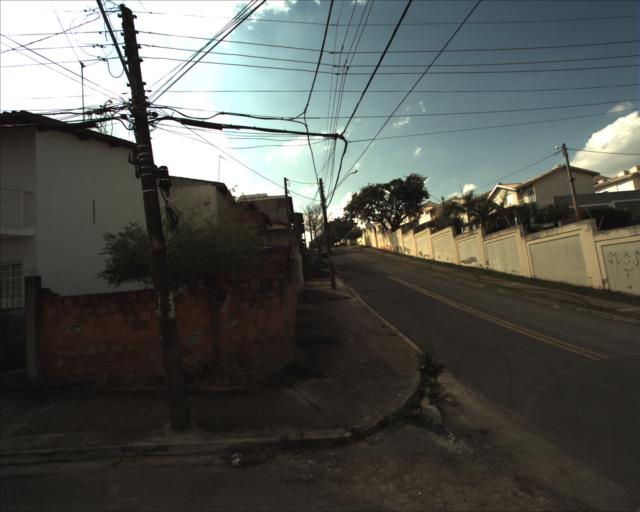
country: BR
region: Sao Paulo
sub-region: Sorocaba
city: Sorocaba
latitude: -23.5089
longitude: -47.4917
